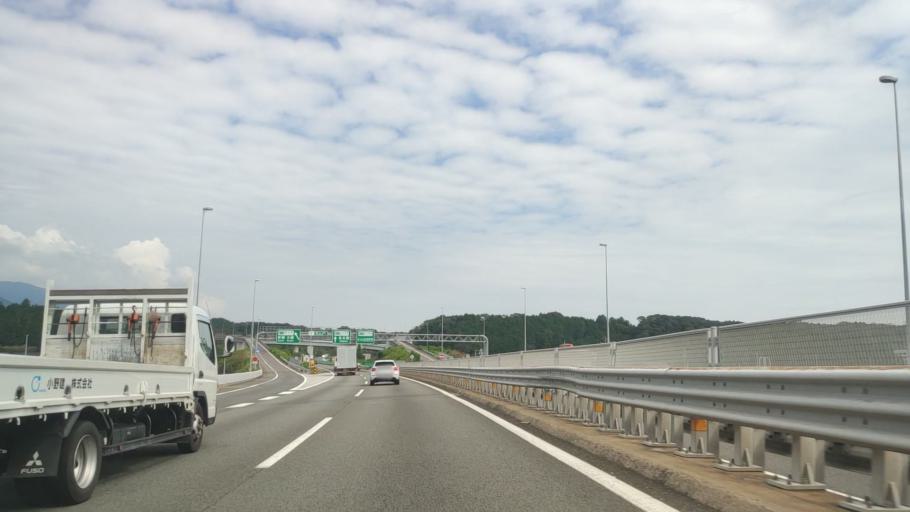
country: JP
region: Mie
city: Kameyama
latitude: 34.8903
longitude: 136.4552
